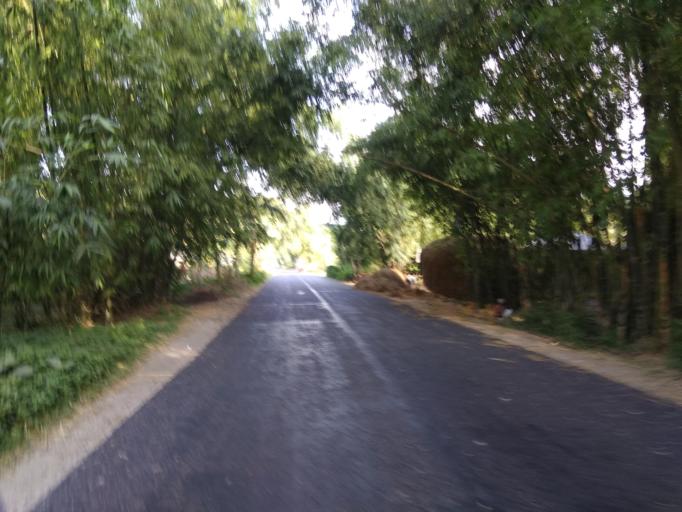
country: BD
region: Rangpur Division
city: Rangpur
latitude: 25.8322
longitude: 89.1176
